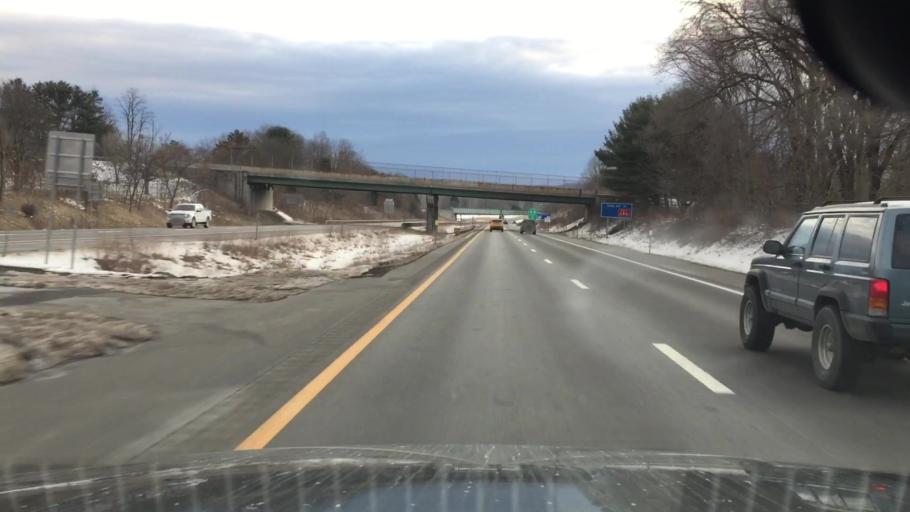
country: US
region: Pennsylvania
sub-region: Bradford County
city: South Waverly
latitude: 41.9993
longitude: -76.5363
